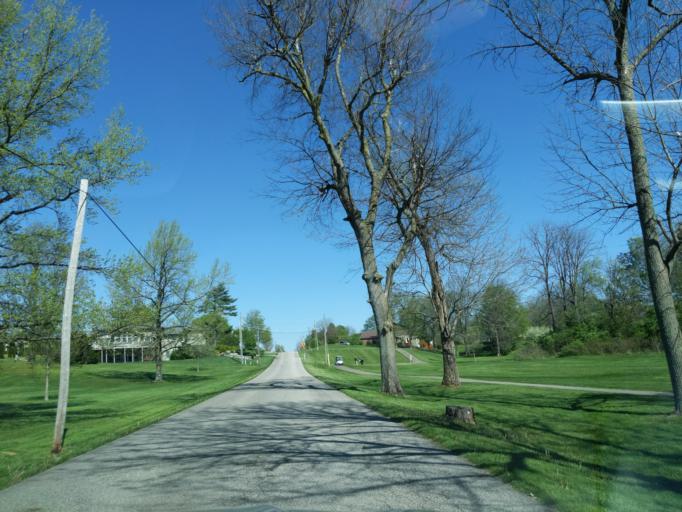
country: US
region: Indiana
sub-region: Decatur County
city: Greensburg
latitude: 39.3289
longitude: -85.5111
